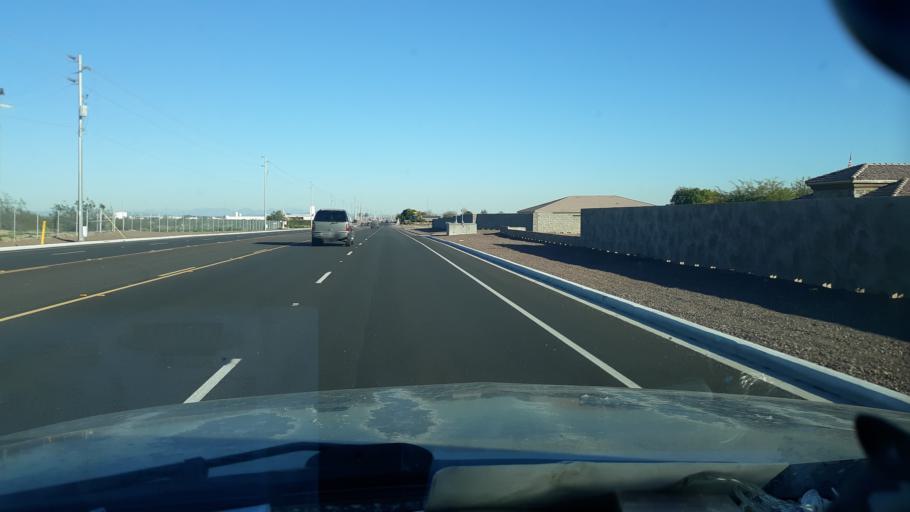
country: US
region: Arizona
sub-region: Maricopa County
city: Citrus Park
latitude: 33.5662
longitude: -112.4376
